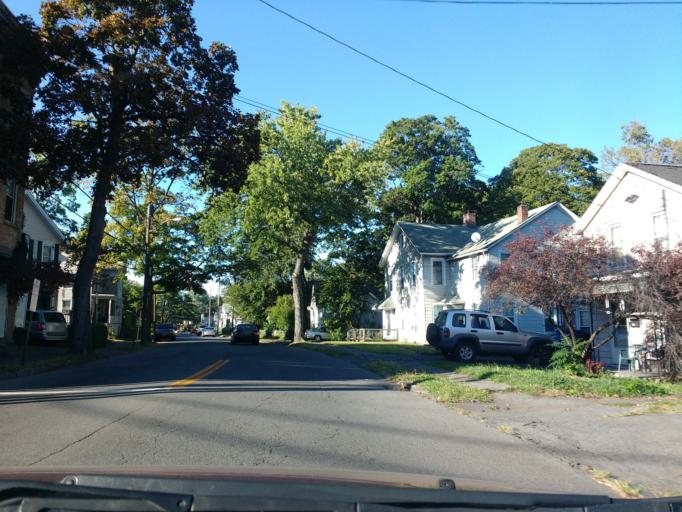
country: US
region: New York
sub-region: Ulster County
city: Kingston
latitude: 41.9276
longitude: -73.9943
